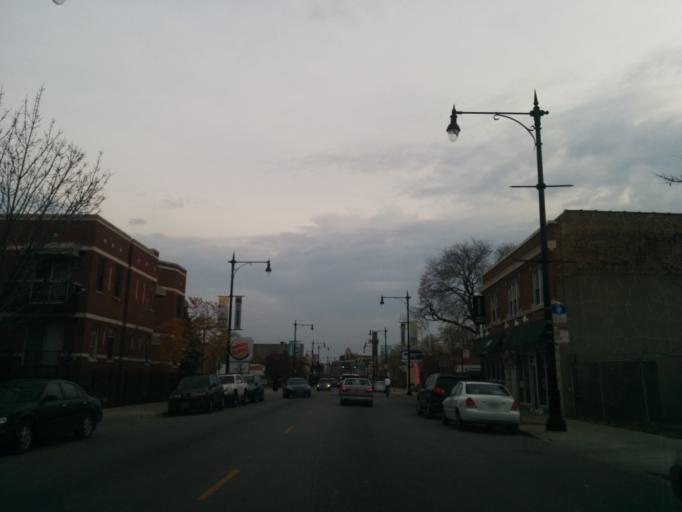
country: US
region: Illinois
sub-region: Cook County
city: Lincolnwood
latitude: 41.9563
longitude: -87.7510
